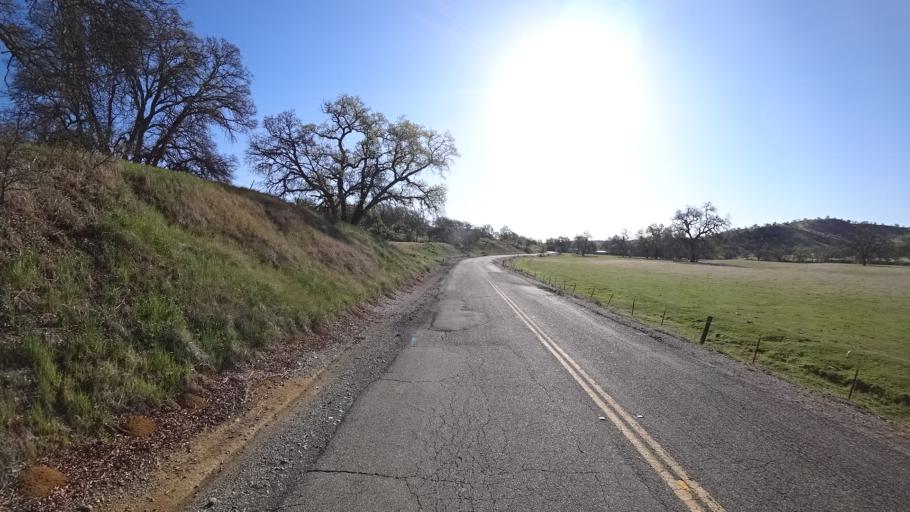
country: US
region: California
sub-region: Tehama County
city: Rancho Tehama Reserve
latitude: 39.7905
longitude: -122.5052
